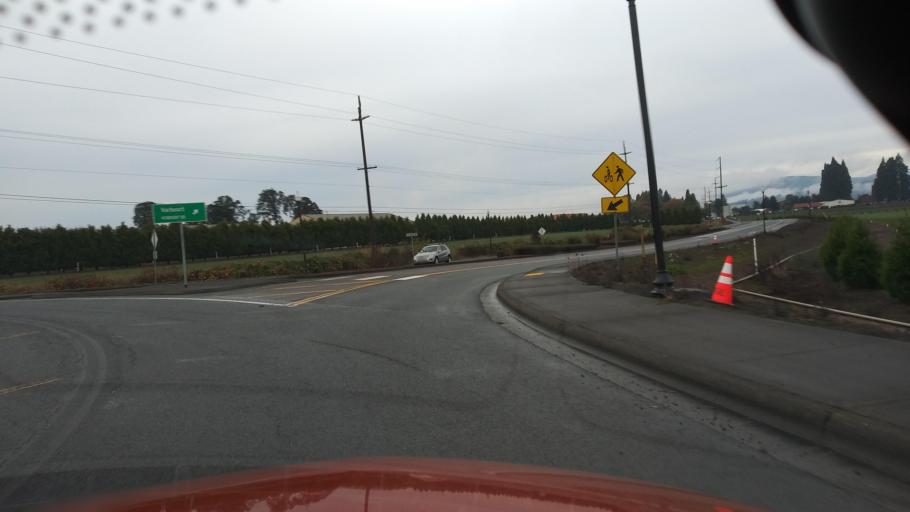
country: US
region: Oregon
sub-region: Washington County
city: Cornelius
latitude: 45.5518
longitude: -123.0736
